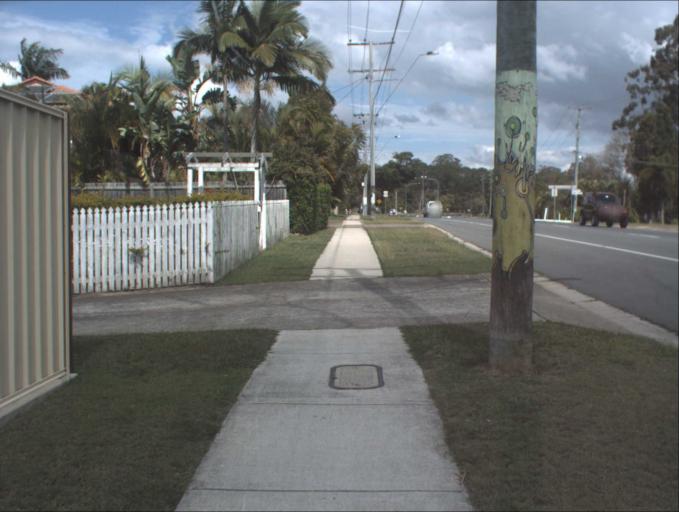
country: AU
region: Queensland
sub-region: Logan
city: Park Ridge South
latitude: -27.6938
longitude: 153.0117
